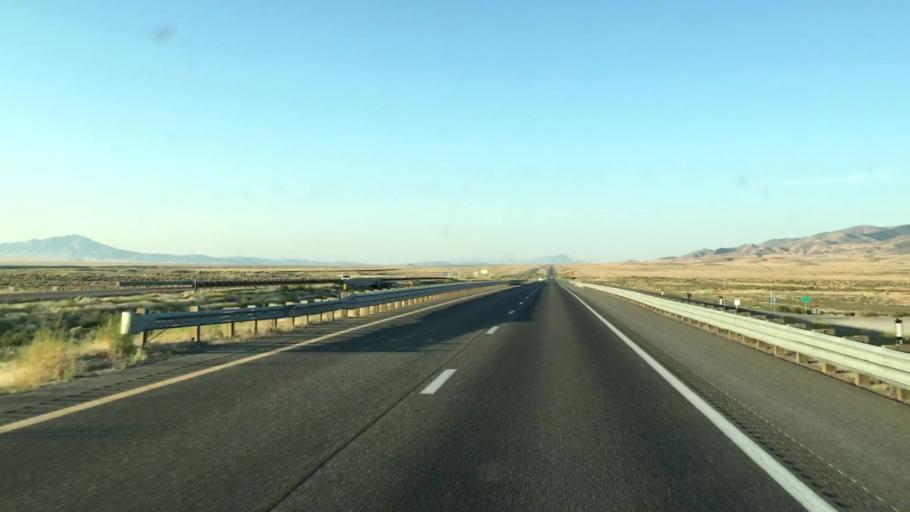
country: US
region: Nevada
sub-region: Humboldt County
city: Winnemucca
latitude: 40.6983
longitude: -118.0514
